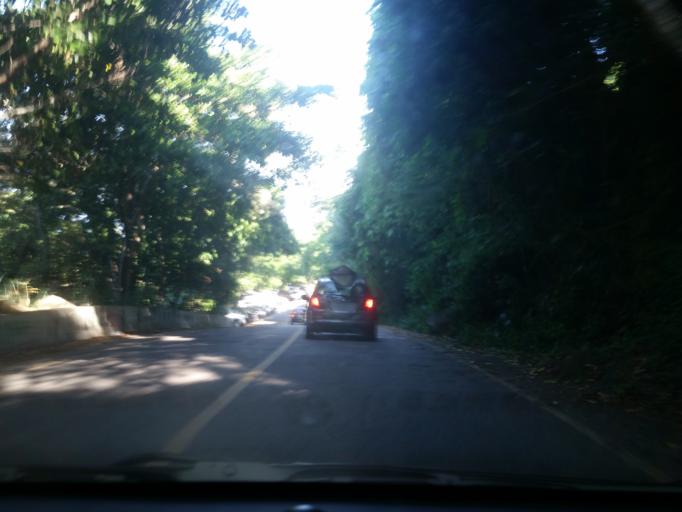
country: BR
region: Rio de Janeiro
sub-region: Nilopolis
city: Nilopolis
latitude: -23.0475
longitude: -43.5136
